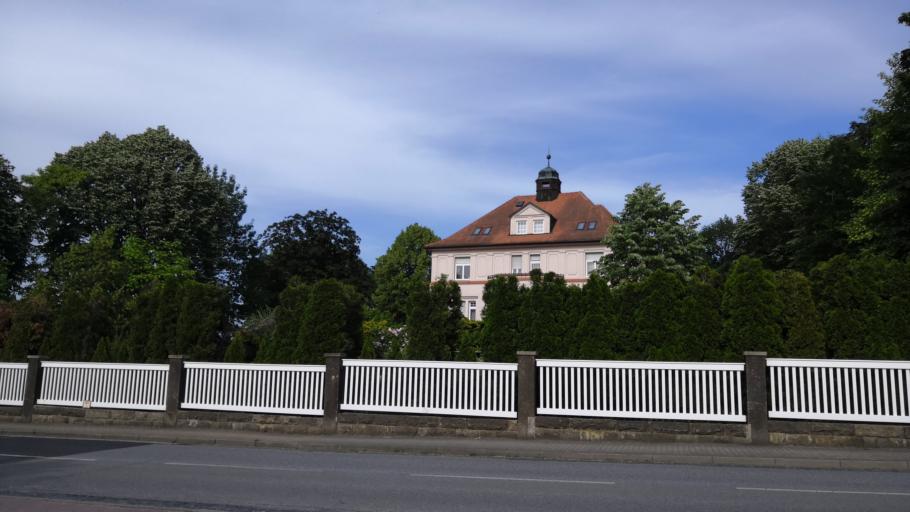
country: DE
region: Saxony
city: Radeberg
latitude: 51.1051
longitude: 13.9219
